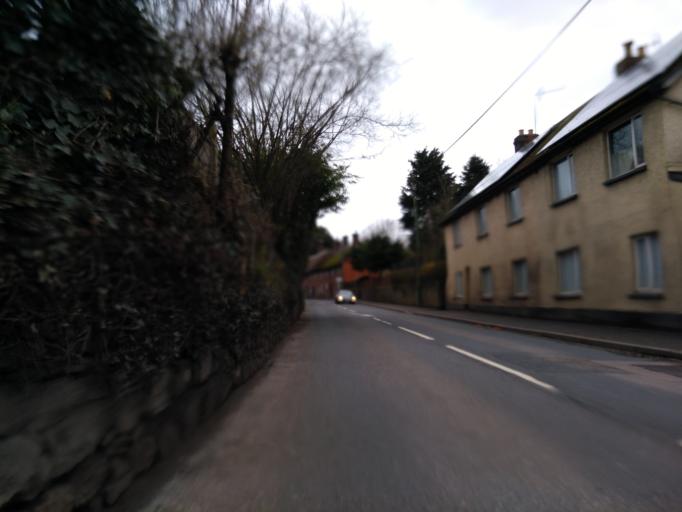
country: GB
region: England
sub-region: Devon
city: Crediton
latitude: 50.7848
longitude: -3.6472
